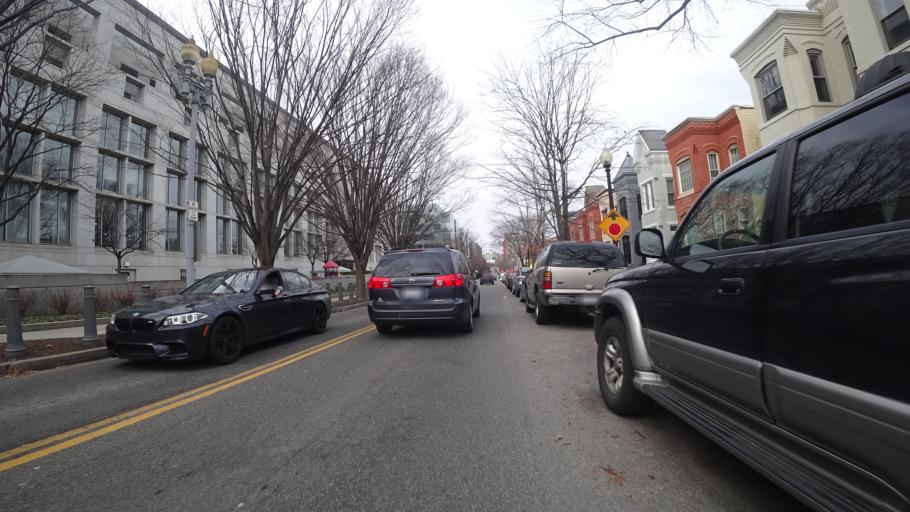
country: US
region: Washington, D.C.
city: Washington, D.C.
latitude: 38.8963
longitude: -77.0035
